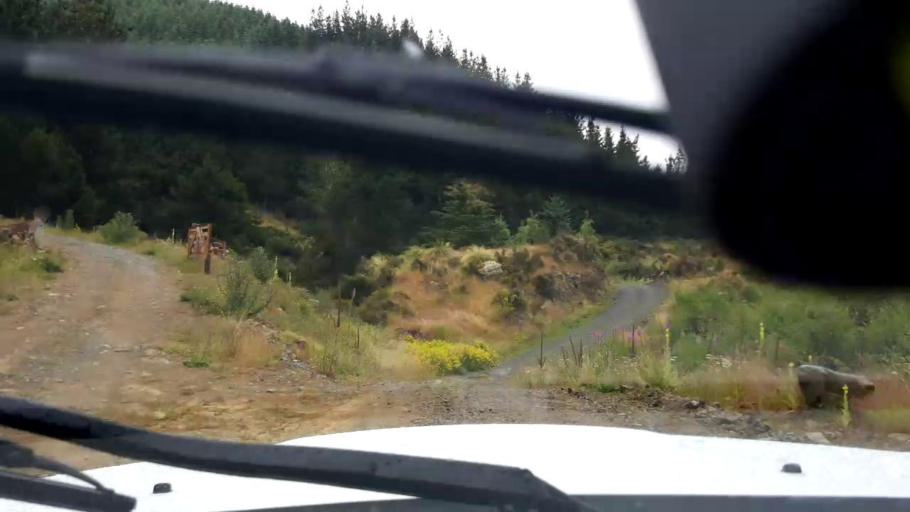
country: NZ
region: Canterbury
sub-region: Timaru District
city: Pleasant Point
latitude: -44.0333
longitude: 170.9910
